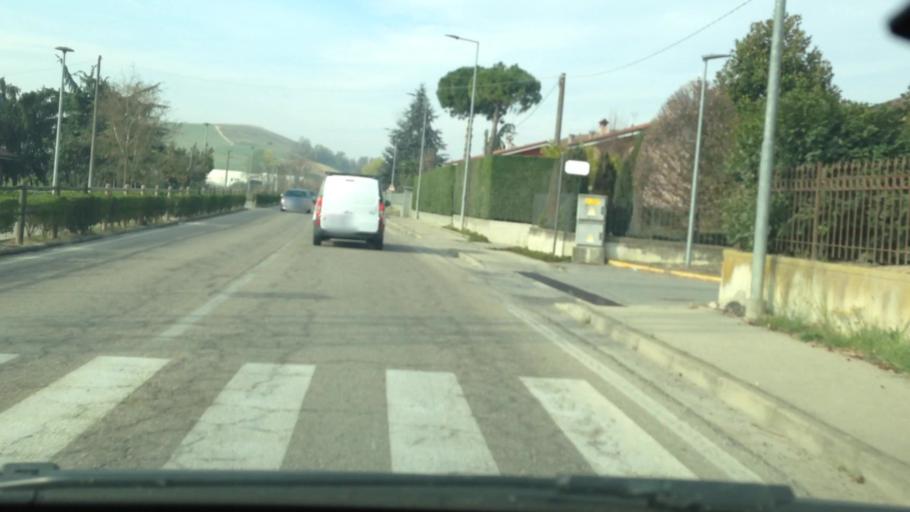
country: IT
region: Piedmont
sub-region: Provincia di Cuneo
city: Canale
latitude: 44.8015
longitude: 8.0168
